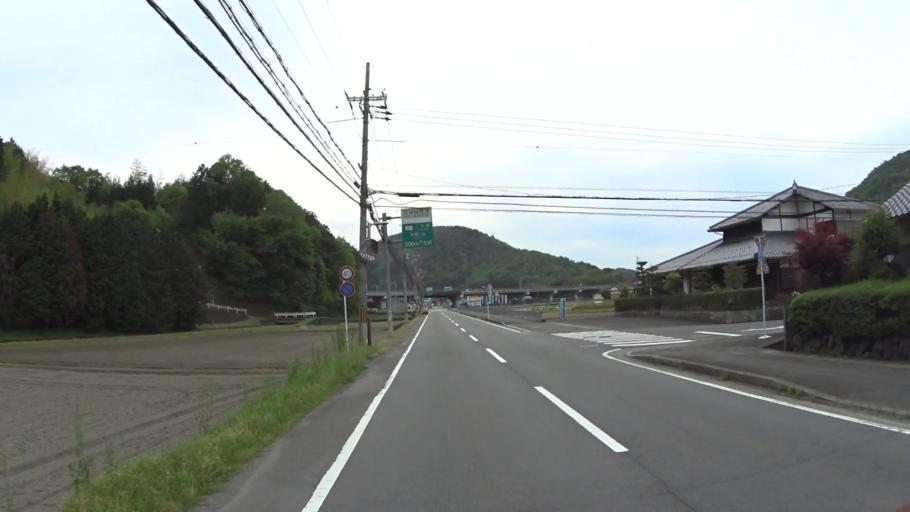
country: JP
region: Kyoto
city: Kameoka
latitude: 35.0928
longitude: 135.5031
